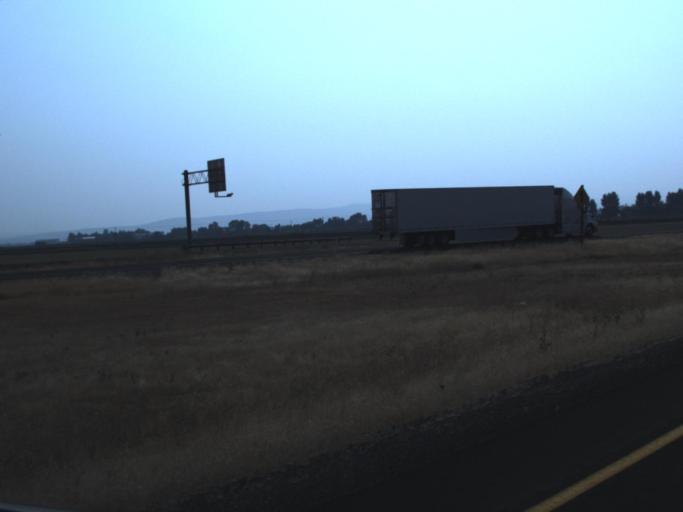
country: US
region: Washington
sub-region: Kittitas County
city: Ellensburg
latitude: 46.9648
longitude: -120.5088
